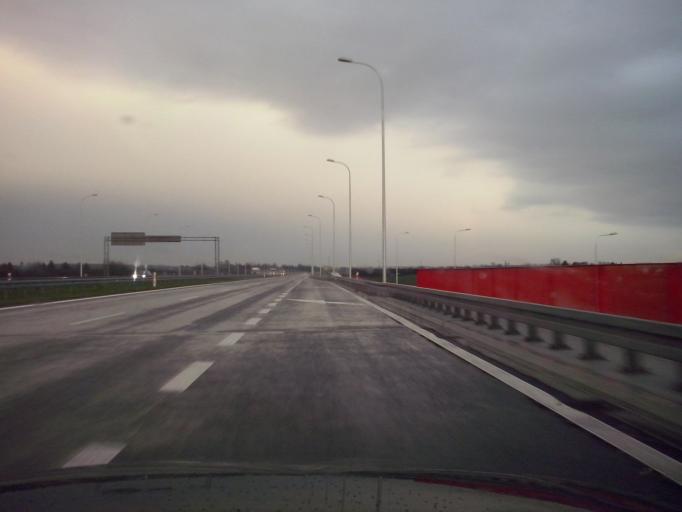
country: PL
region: Lublin Voivodeship
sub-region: Powiat lubelski
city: Jastkow
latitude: 51.2804
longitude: 22.4624
